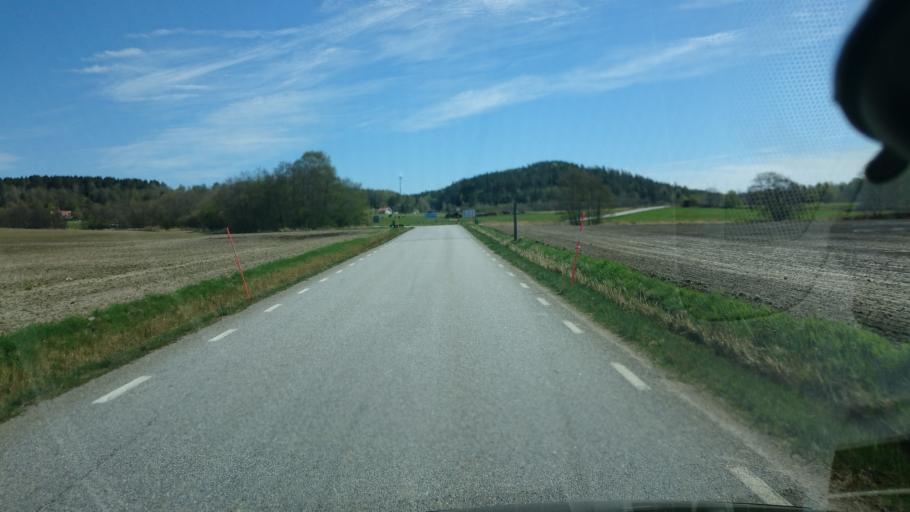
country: SE
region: Vaestra Goetaland
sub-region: Munkedals Kommun
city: Munkedal
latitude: 58.3787
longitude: 11.6751
